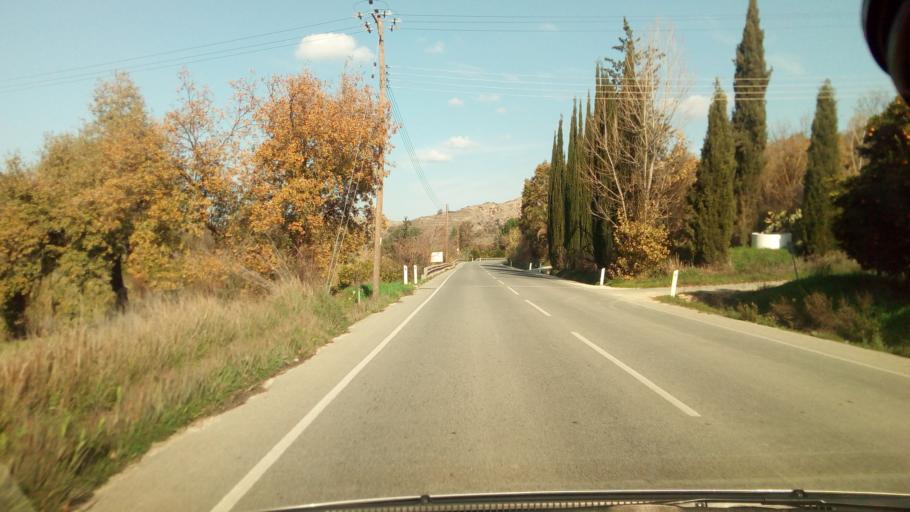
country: CY
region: Pafos
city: Pegeia
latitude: 34.9397
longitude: 32.4692
